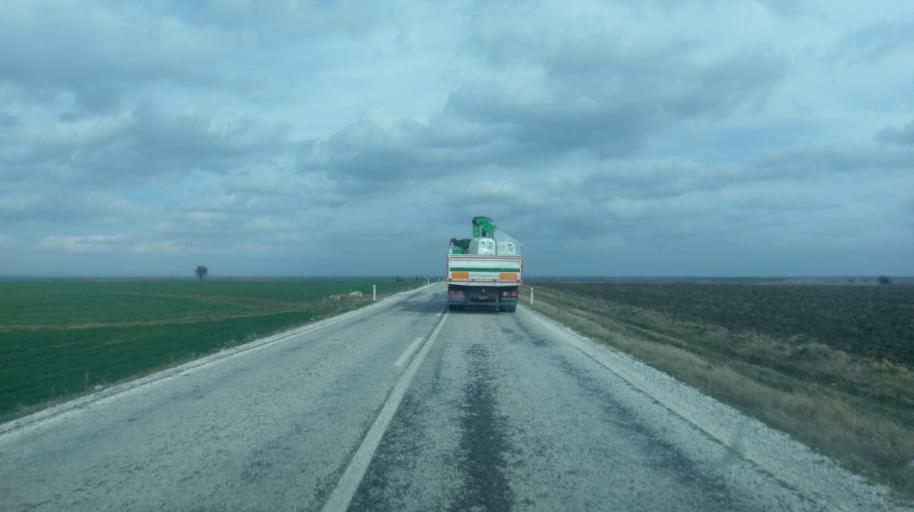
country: TR
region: Edirne
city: Haskoy
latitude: 41.6552
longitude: 26.9078
